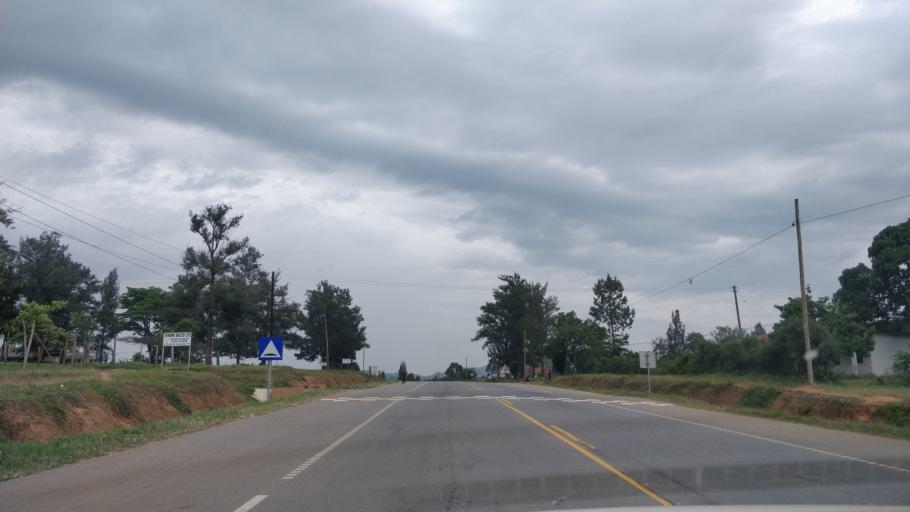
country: UG
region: Western Region
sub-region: Sheema District
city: Kibingo
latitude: -0.6587
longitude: 30.4651
